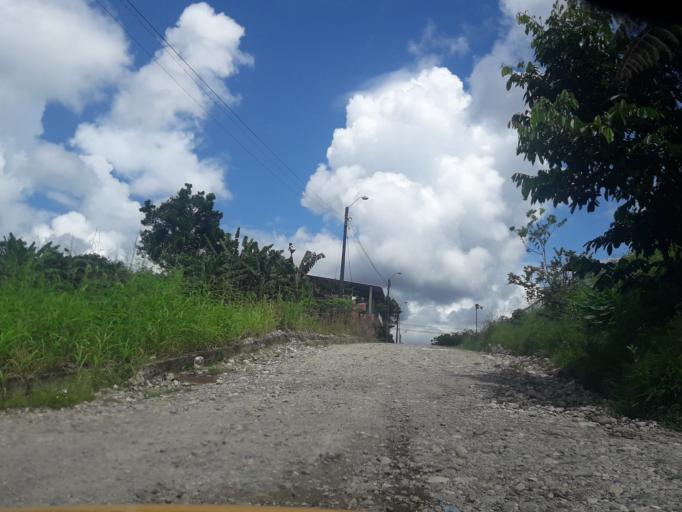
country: EC
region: Napo
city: Tena
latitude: -1.0036
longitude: -77.8195
